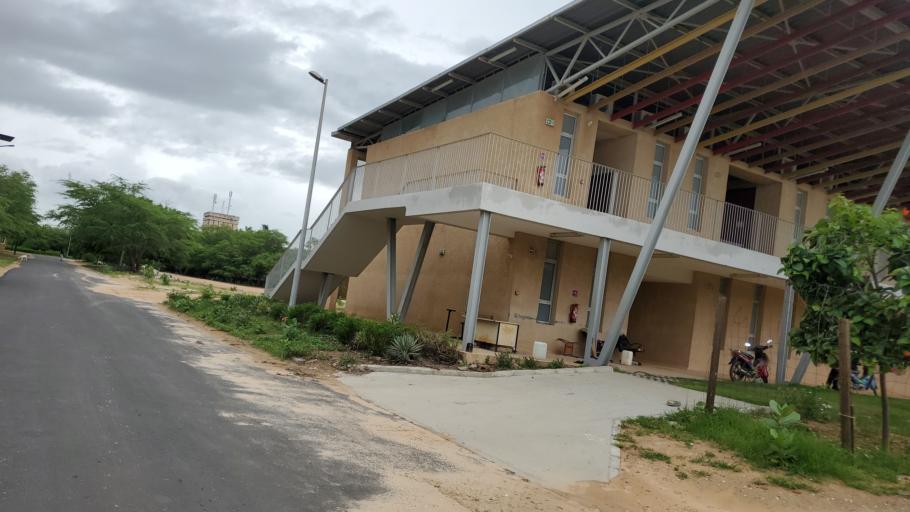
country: SN
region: Saint-Louis
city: Saint-Louis
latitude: 16.0630
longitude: -16.4193
